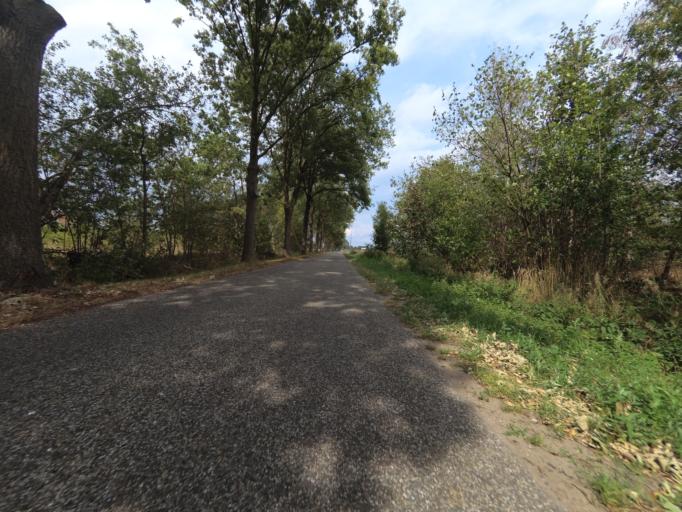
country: NL
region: Overijssel
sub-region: Gemeente Hof van Twente
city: Delden
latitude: 52.2191
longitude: 6.7423
